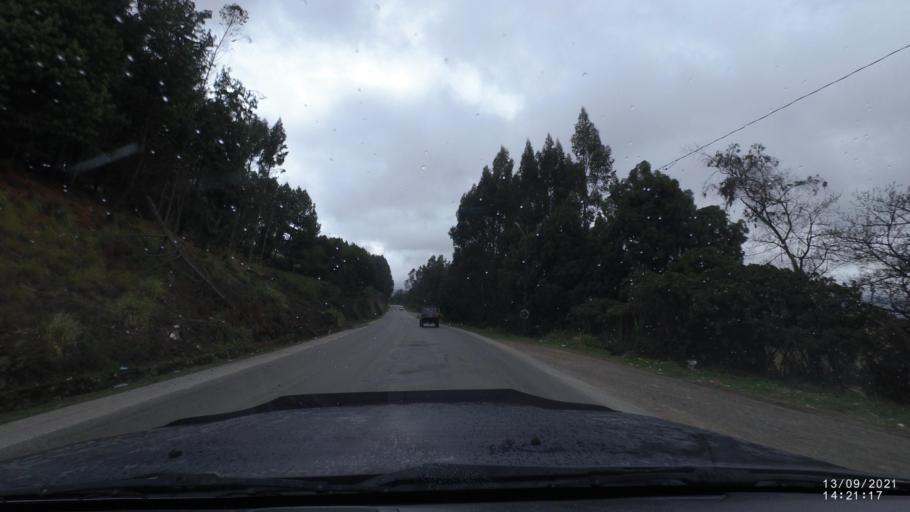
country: BO
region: Cochabamba
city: Colomi
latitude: -17.2582
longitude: -65.8907
